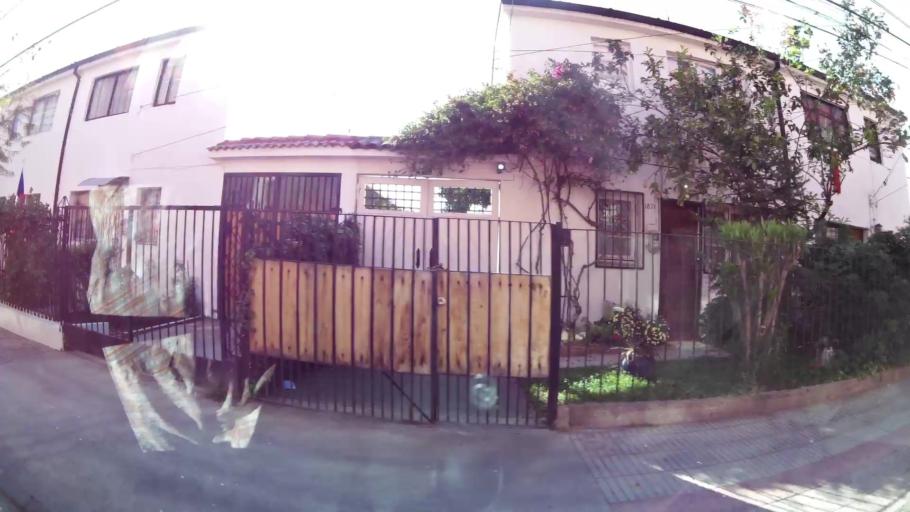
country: CL
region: Santiago Metropolitan
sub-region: Provincia de Santiago
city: Santiago
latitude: -33.4098
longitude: -70.6617
